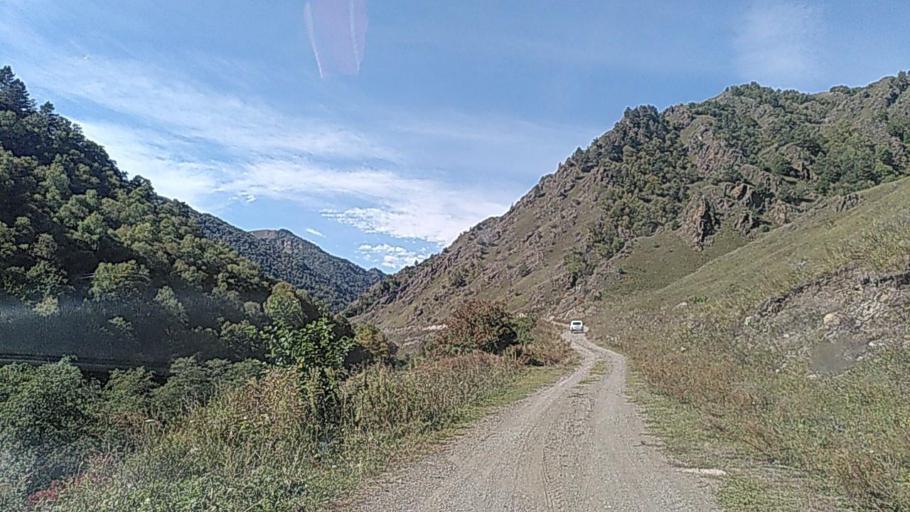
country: RU
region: Kabardino-Balkariya
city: Kamennomostskoye
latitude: 43.7228
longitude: 42.8494
